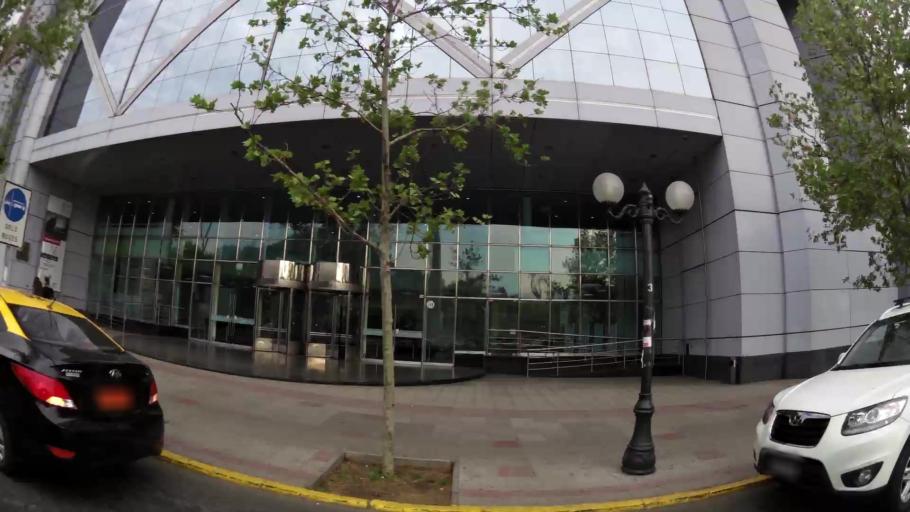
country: CL
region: Santiago Metropolitan
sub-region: Provincia de Santiago
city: Santiago
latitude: -33.4369
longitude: -70.6326
